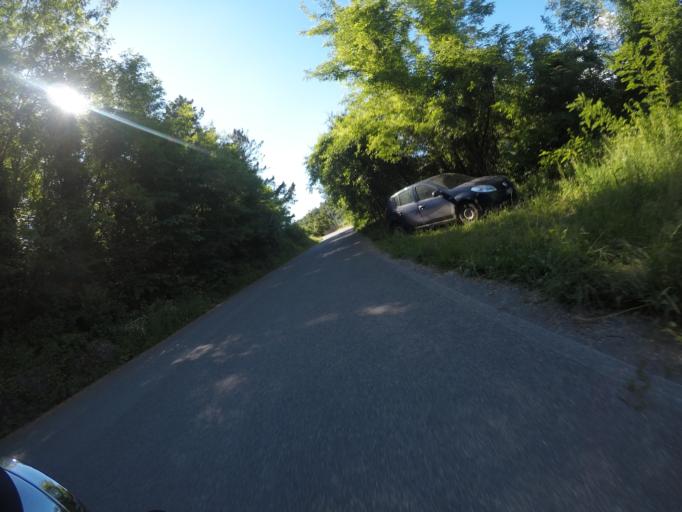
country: IT
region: Tuscany
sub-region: Provincia di Massa-Carrara
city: Fosdinovo
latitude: 44.1437
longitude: 10.0738
